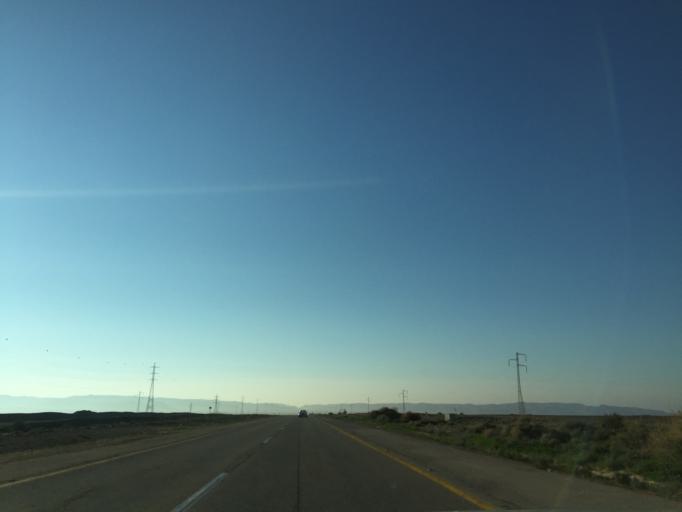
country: IL
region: Southern District
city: Mitzpe Ramon
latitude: 30.4348
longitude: 34.9398
